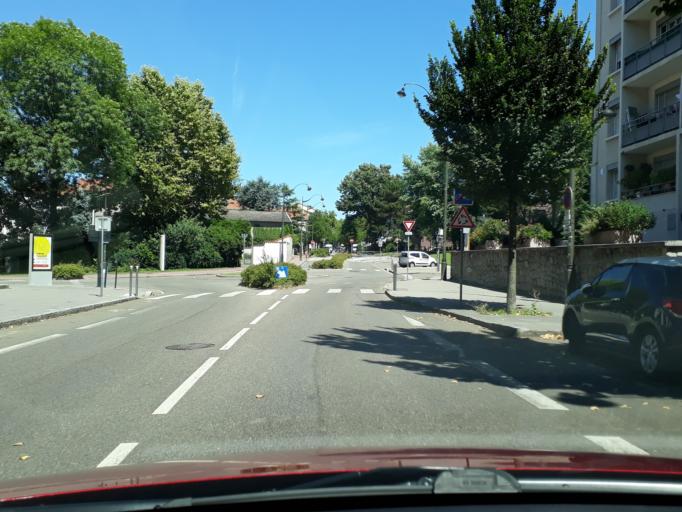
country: FR
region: Rhone-Alpes
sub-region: Departement du Rhone
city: Saint-Priest
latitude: 45.6964
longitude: 4.9418
